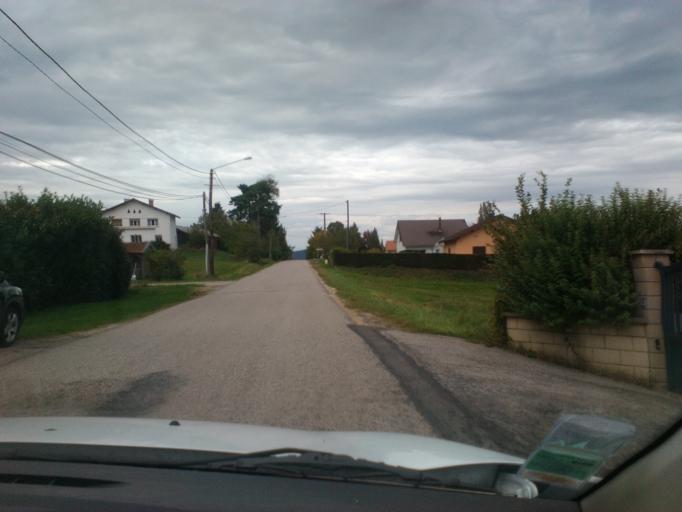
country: FR
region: Lorraine
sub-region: Departement des Vosges
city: Saint-Michel-sur-Meurthe
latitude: 48.3198
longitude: 6.8544
